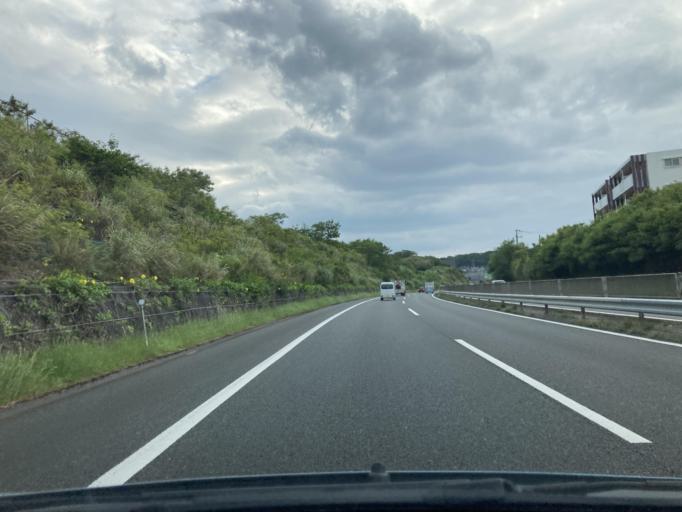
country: JP
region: Okinawa
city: Ginowan
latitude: 26.2511
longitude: 127.7604
